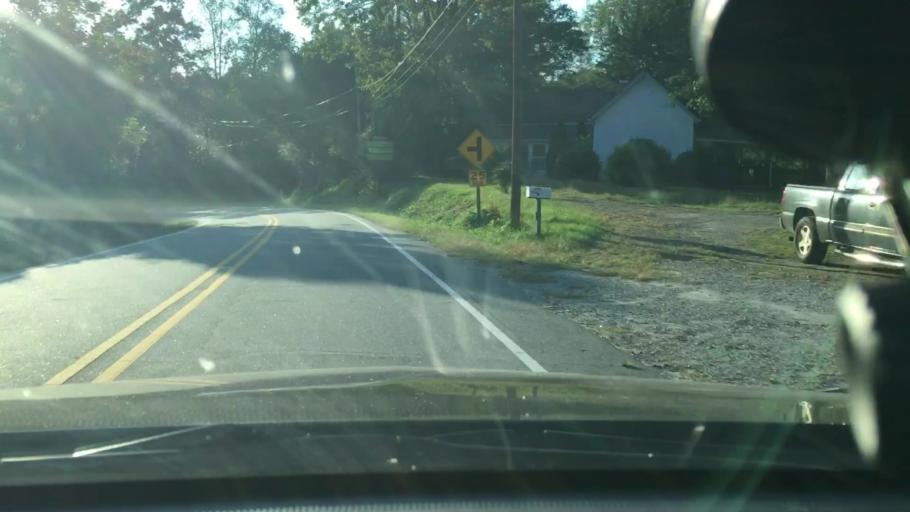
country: US
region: North Carolina
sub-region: Rutherford County
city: Rutherfordton
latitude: 35.3639
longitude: -81.9696
